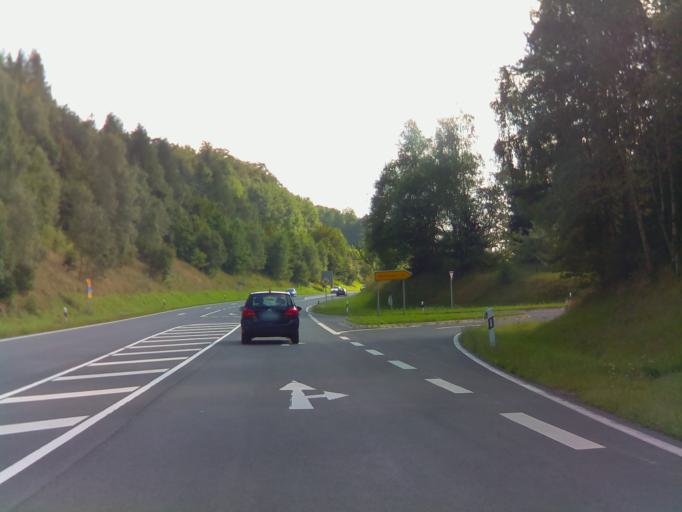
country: DE
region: Bavaria
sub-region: Regierungsbezirk Unterfranken
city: Wildflecken
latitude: 50.3661
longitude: 9.8963
